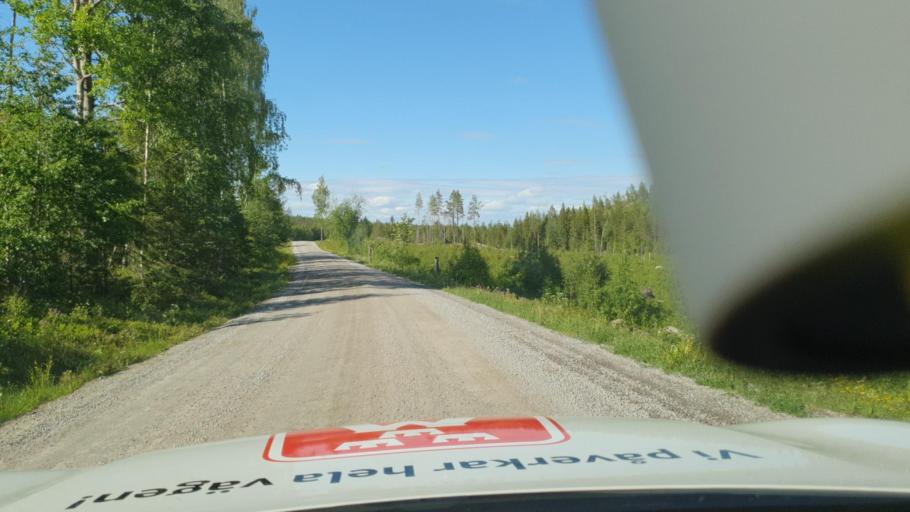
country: SE
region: Vaesterbotten
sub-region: Vannas Kommun
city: Vaennaes
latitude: 63.7902
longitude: 19.6250
